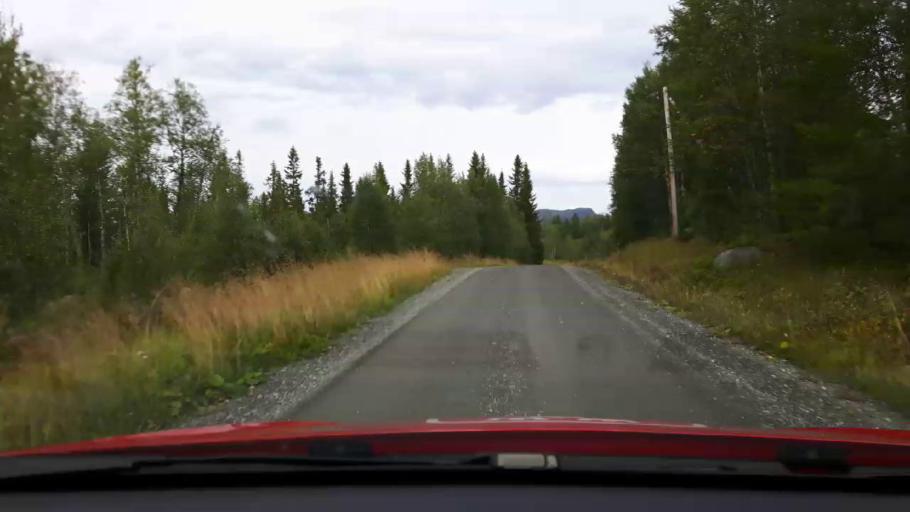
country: SE
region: Jaemtland
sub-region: Are Kommun
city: Are
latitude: 63.7629
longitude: 13.0917
